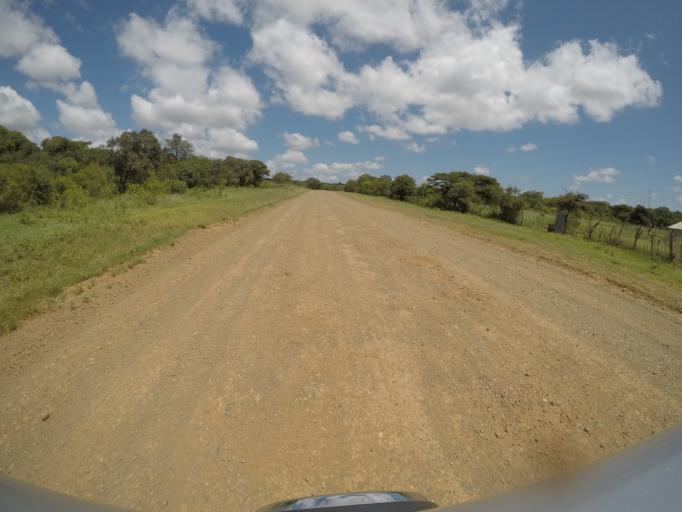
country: ZA
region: KwaZulu-Natal
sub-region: uThungulu District Municipality
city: Empangeni
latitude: -28.5965
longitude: 31.8298
